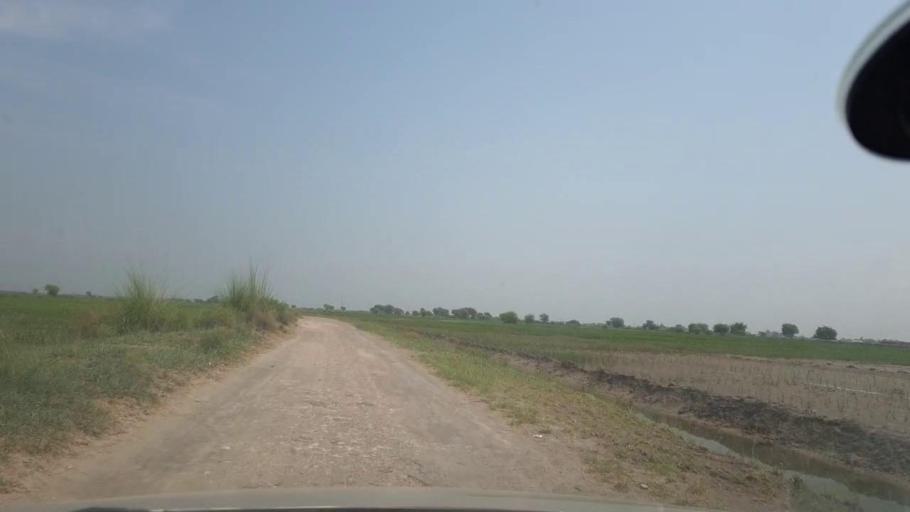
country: PK
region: Sindh
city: Jacobabad
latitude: 28.1395
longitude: 68.3663
